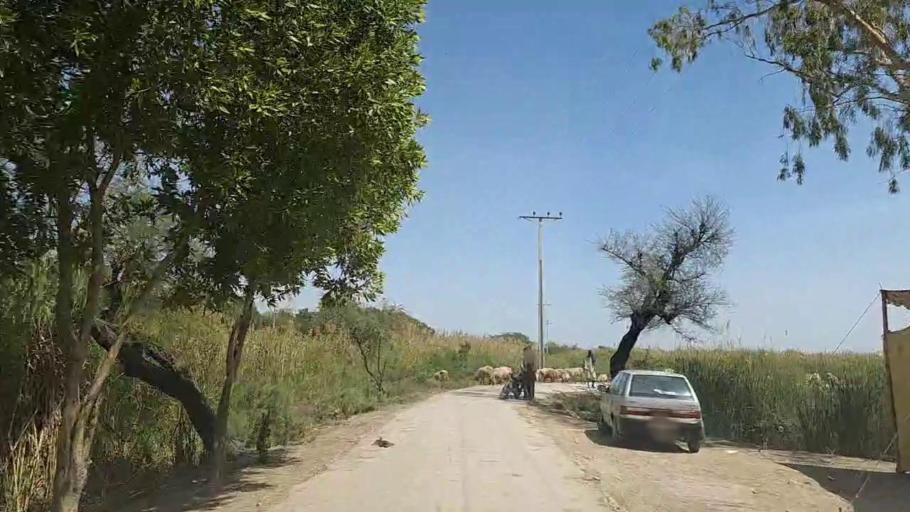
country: PK
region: Sindh
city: Thatta
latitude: 24.7865
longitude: 67.7551
